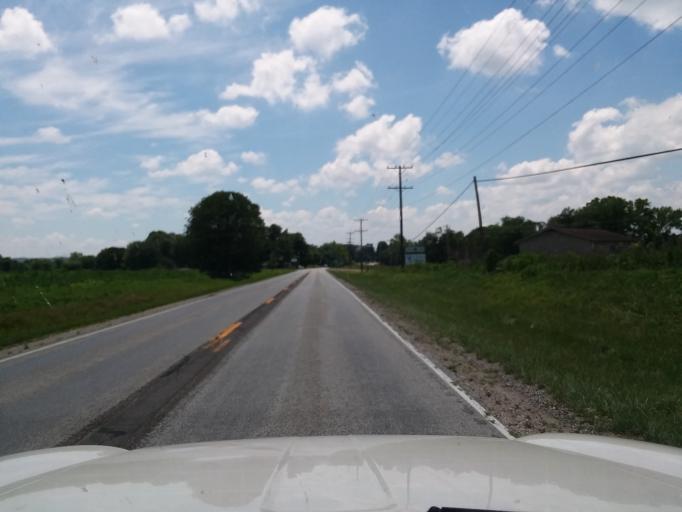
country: US
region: Indiana
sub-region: Johnson County
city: Trafalgar
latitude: 39.3760
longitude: -86.2500
